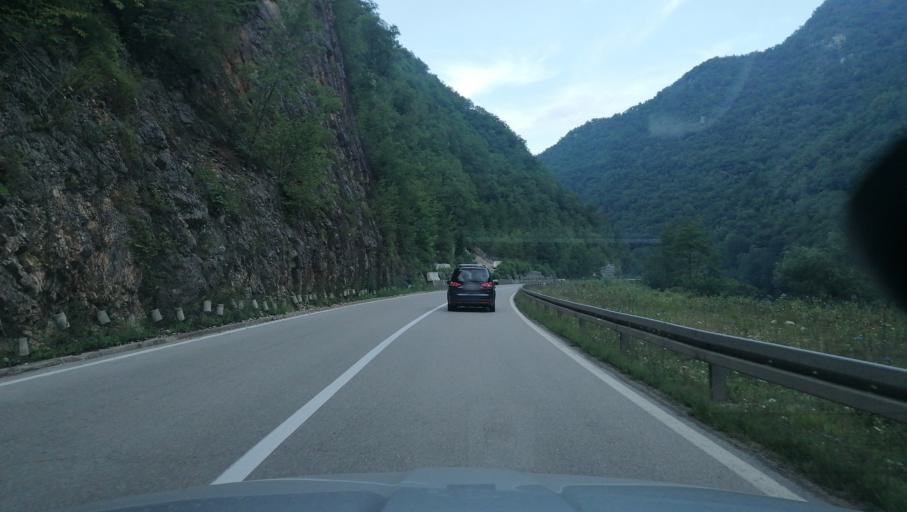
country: BA
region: Federation of Bosnia and Herzegovina
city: Jajce
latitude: 44.4421
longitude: 17.2346
